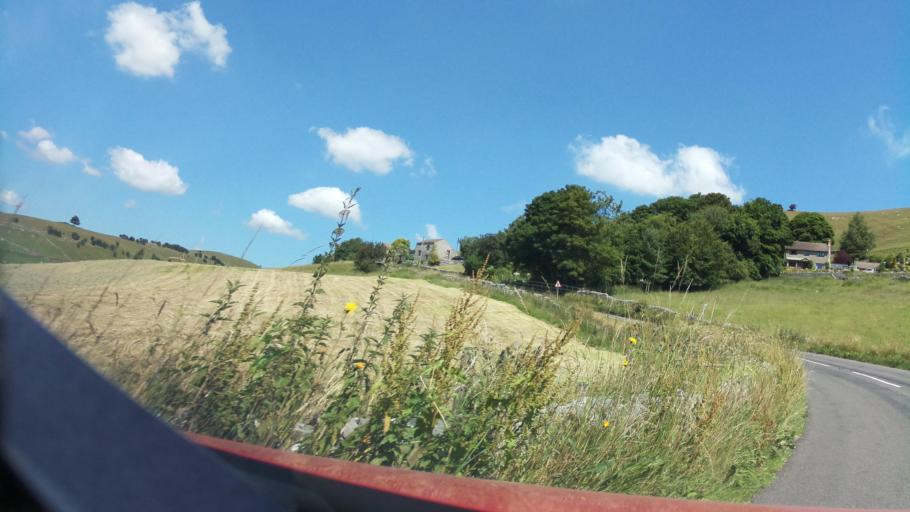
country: GB
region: England
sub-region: Derbyshire
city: Buxton
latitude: 53.2036
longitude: -1.8688
